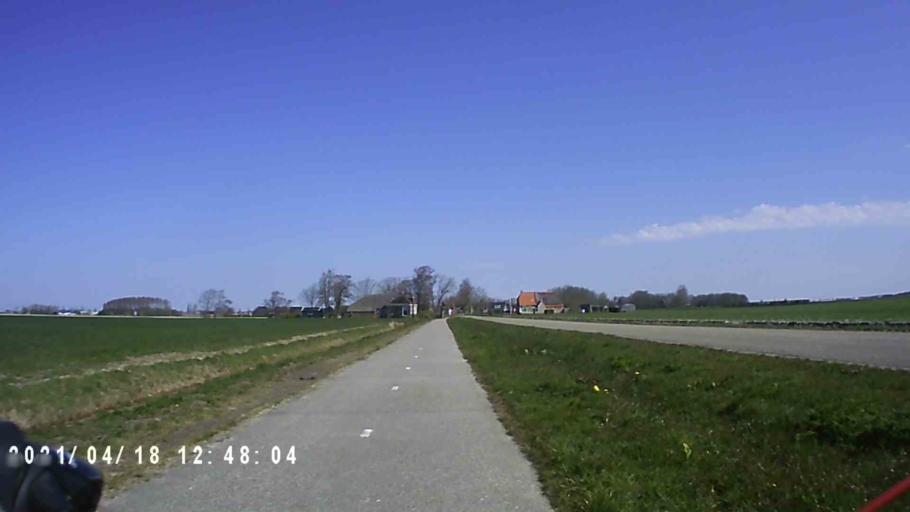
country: NL
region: Friesland
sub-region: Gemeente Dongeradeel
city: Dokkum
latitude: 53.3721
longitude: 6.0507
